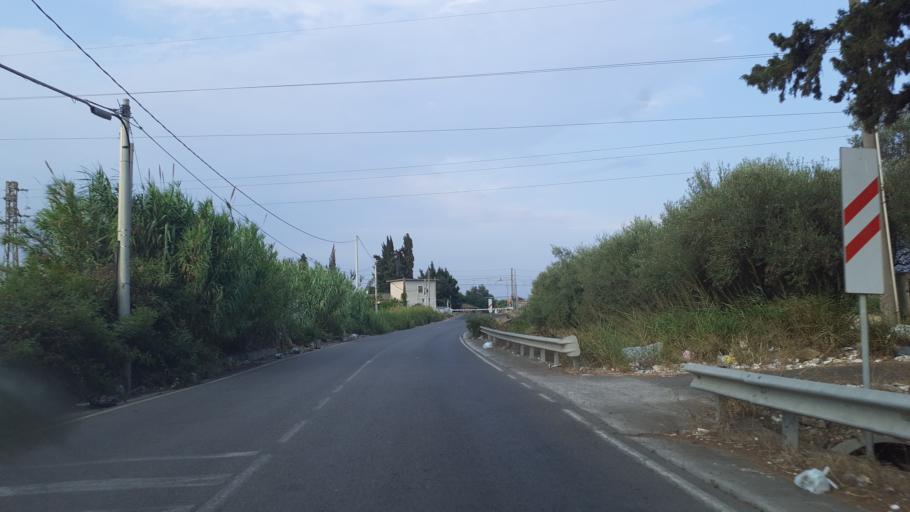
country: IT
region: Sicily
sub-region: Catania
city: Catania
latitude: 37.4549
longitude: 15.0283
